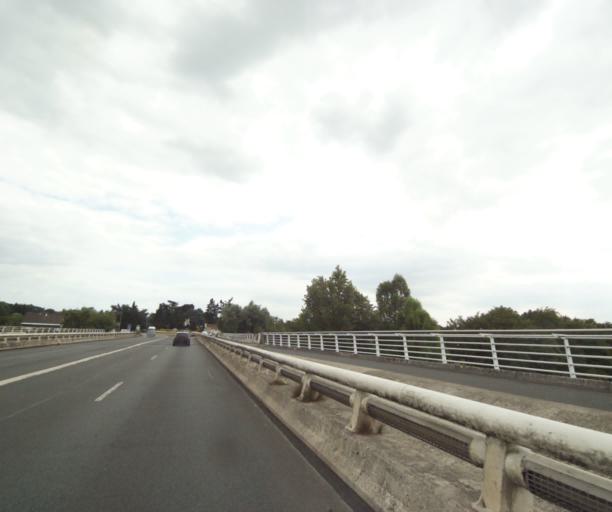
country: FR
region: Centre
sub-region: Departement du Loiret
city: Saint-Pryve-Saint-Mesmin
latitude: 47.8944
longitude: 1.8762
